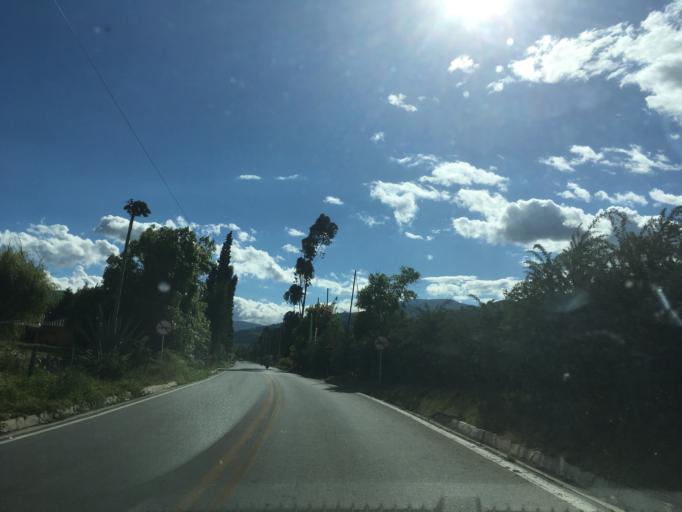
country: CO
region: Boyaca
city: Pesca
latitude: 5.6004
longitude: -73.0264
